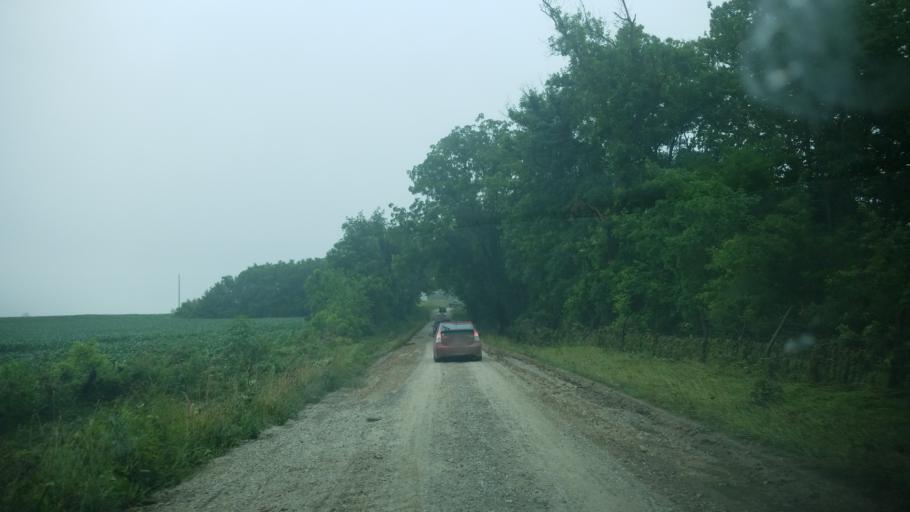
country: US
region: Missouri
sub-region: Pike County
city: Bowling Green
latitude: 39.3082
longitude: -91.2915
